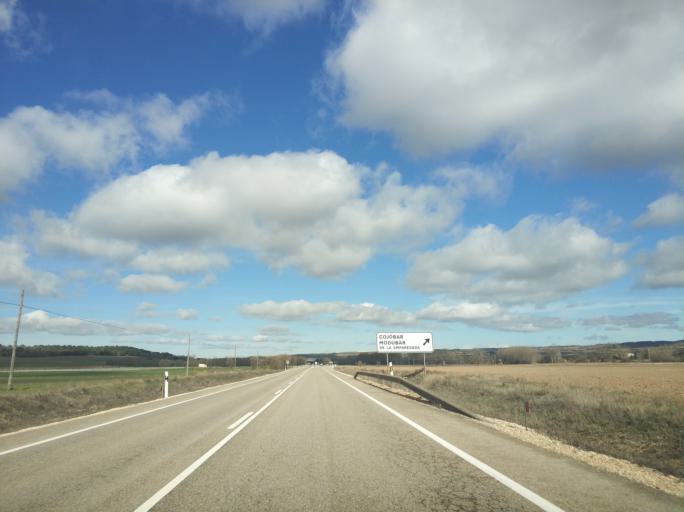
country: ES
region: Castille and Leon
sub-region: Provincia de Burgos
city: Sarracin
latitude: 42.2403
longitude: -3.6728
